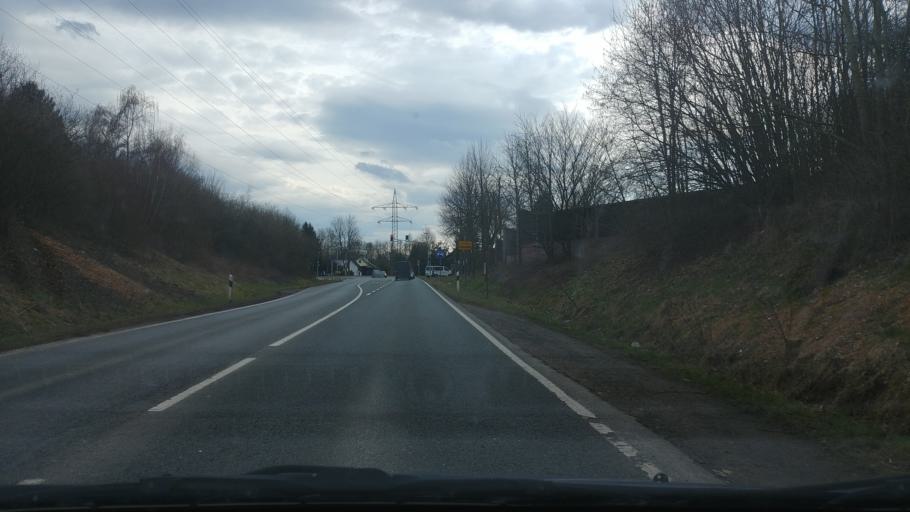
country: DE
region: Lower Saxony
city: Bevern
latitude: 51.8279
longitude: 9.4822
